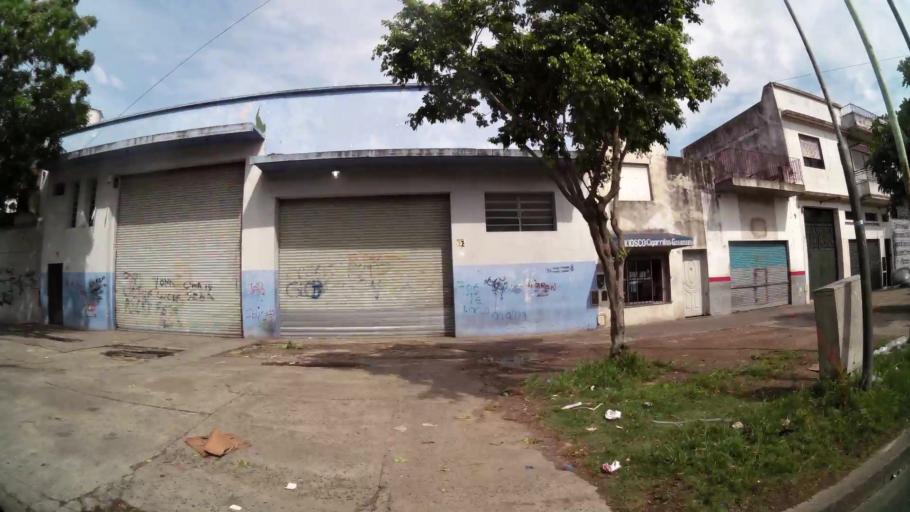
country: AR
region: Buenos Aires F.D.
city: Villa Lugano
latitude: -34.6491
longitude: -58.4294
